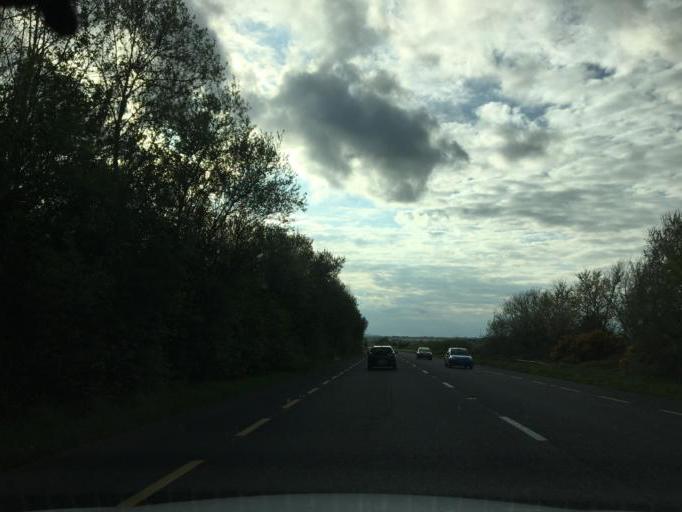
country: IE
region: Leinster
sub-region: Loch Garman
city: Loch Garman
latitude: 52.3446
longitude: -6.5909
